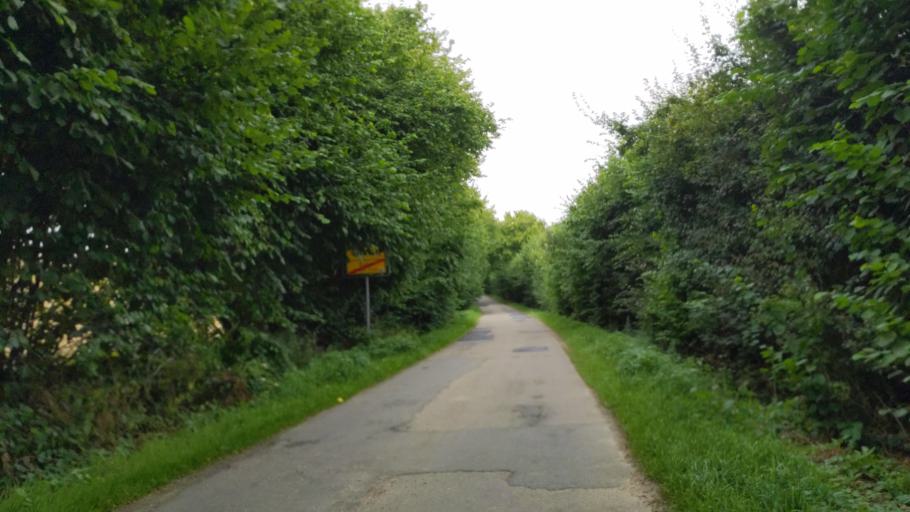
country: DE
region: Schleswig-Holstein
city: Eutin
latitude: 54.1589
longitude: 10.6244
